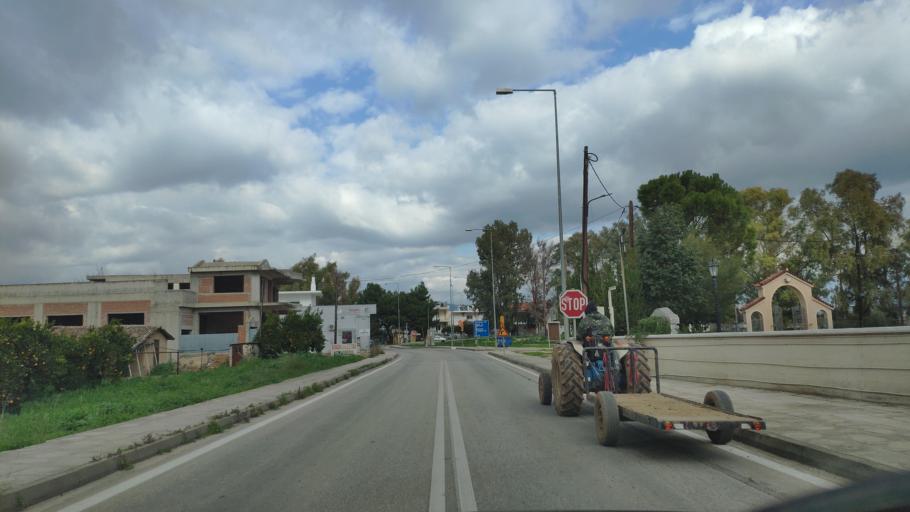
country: GR
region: Peloponnese
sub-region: Nomos Argolidos
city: Argos
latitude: 37.6269
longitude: 22.7375
